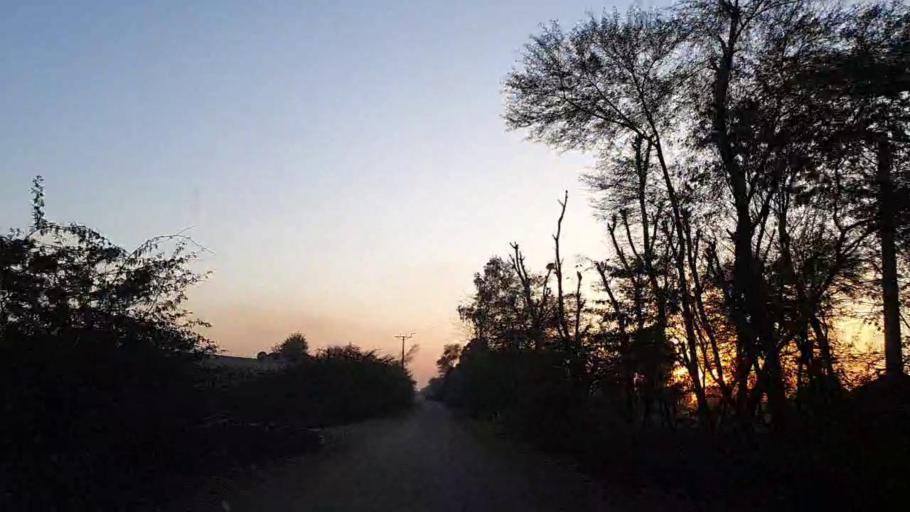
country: PK
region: Sindh
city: Daur
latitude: 26.3491
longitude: 68.3081
